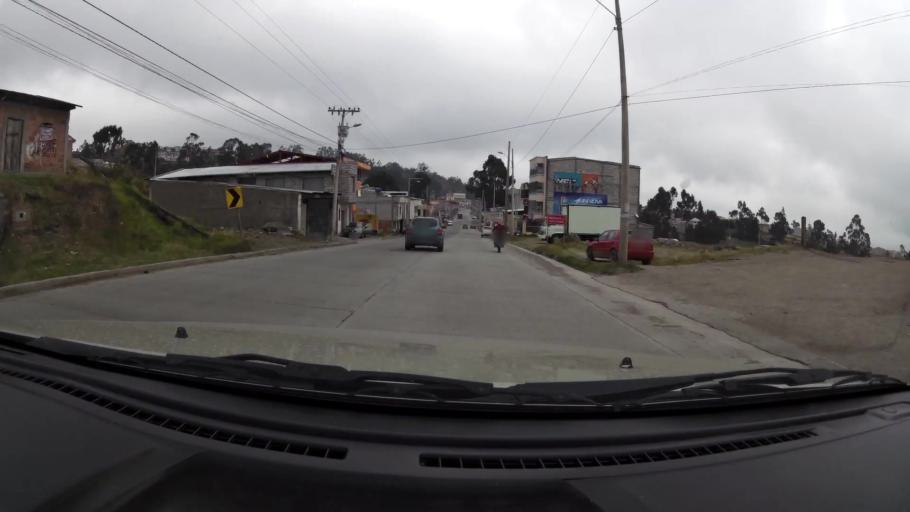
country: EC
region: Canar
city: Canar
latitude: -2.5702
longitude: -78.9328
